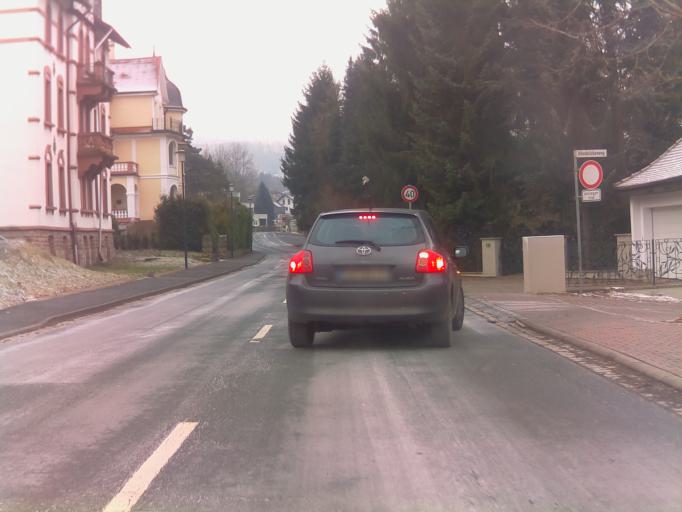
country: DE
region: Bavaria
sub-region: Regierungsbezirk Unterfranken
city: Bad Bruckenau
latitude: 50.2986
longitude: 9.7455
